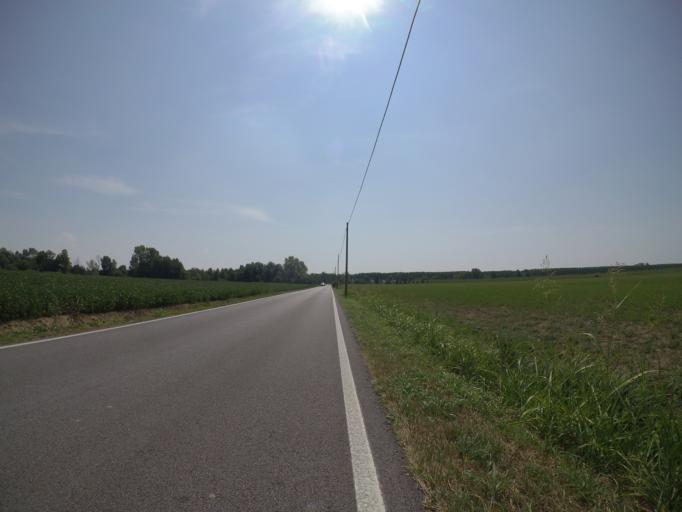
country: IT
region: Friuli Venezia Giulia
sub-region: Provincia di Udine
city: Pocenia
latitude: 45.8500
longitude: 13.0926
